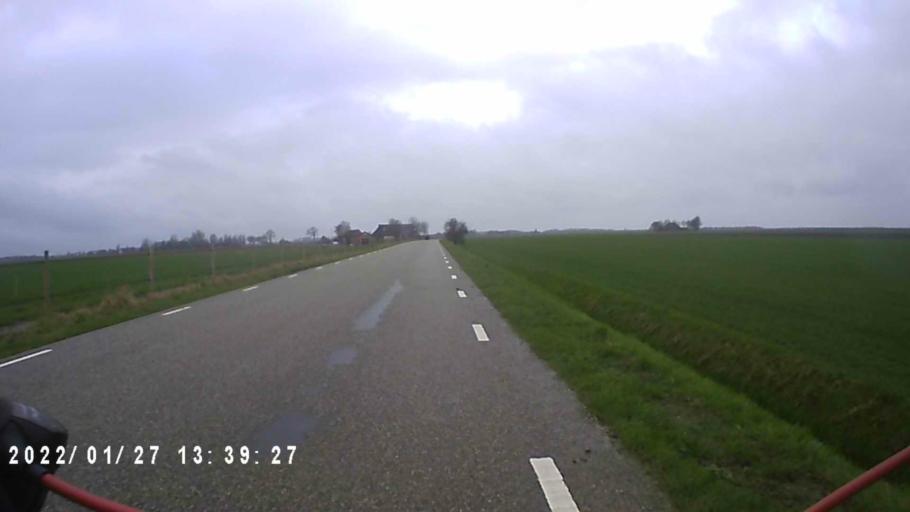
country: NL
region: Friesland
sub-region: Gemeente Kollumerland en Nieuwkruisland
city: Kollum
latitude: 53.2982
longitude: 6.2203
